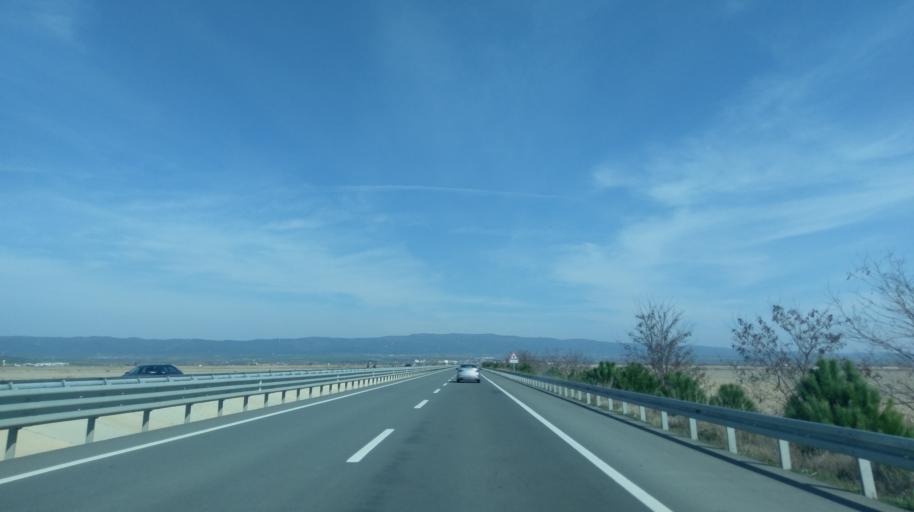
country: TR
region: Canakkale
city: Evrese
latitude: 40.6223
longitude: 26.8678
